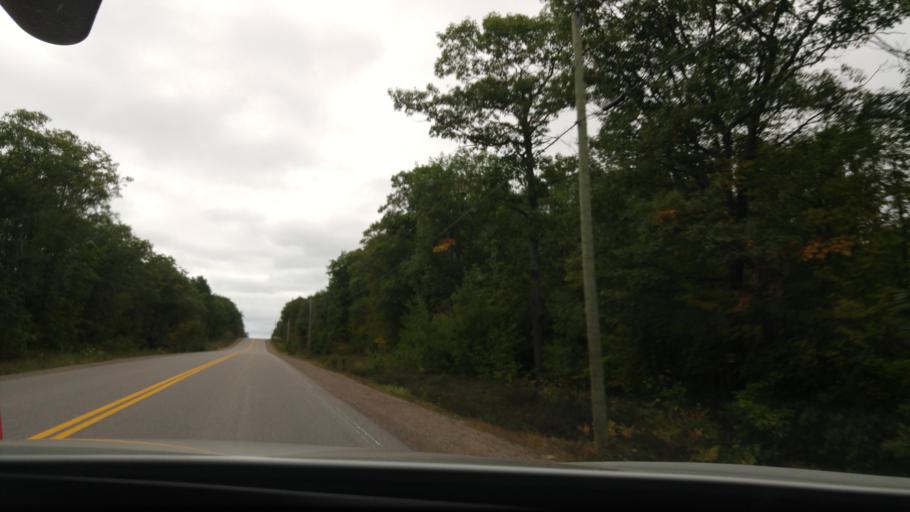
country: CA
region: Ontario
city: Petawawa
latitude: 45.8220
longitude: -77.3004
